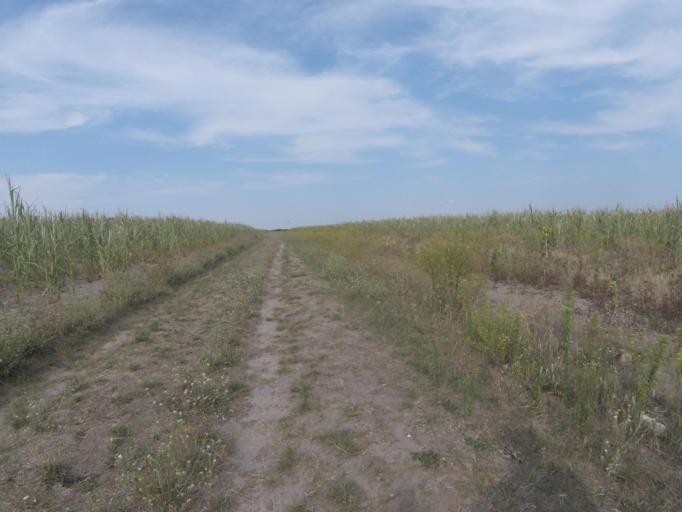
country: DE
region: Brandenburg
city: Bestensee
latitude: 52.3027
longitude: 13.7237
